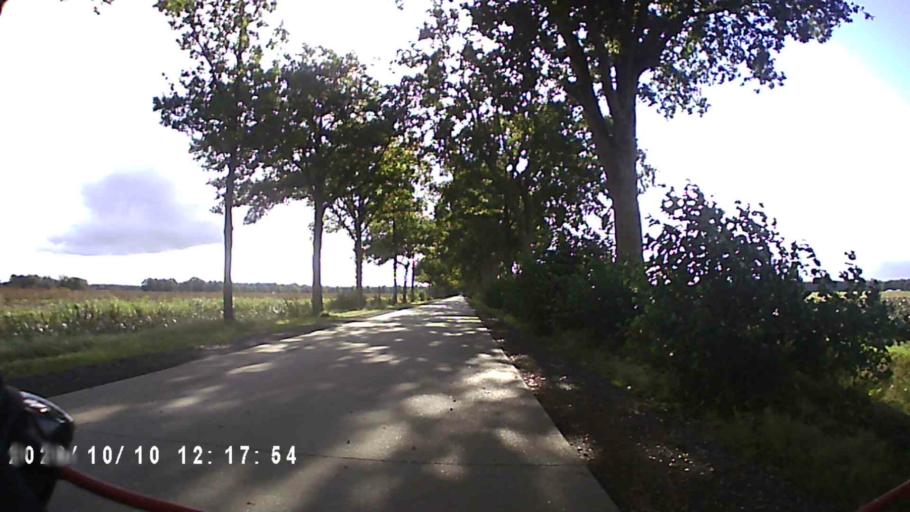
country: NL
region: Friesland
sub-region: Gemeente Heerenveen
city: Jubbega
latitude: 53.0179
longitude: 6.1721
